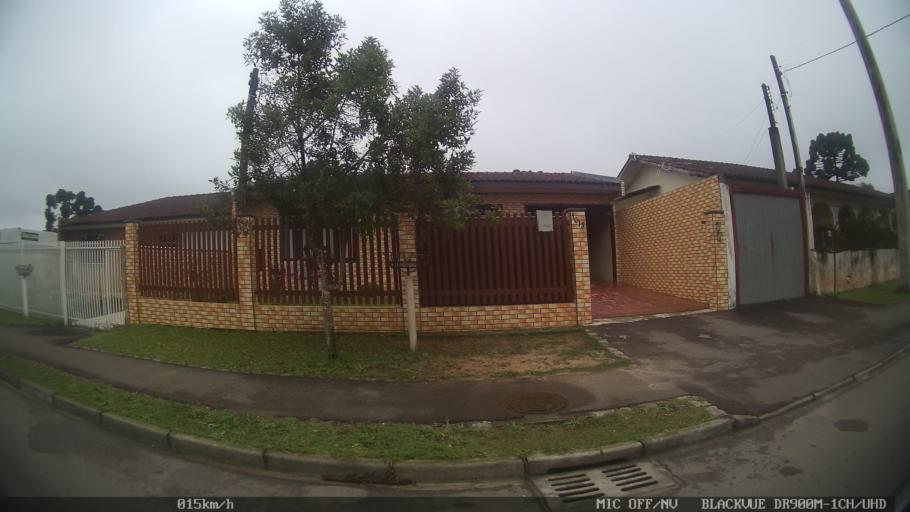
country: BR
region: Parana
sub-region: Sao Jose Dos Pinhais
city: Sao Jose dos Pinhais
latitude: -25.5830
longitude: -49.1707
